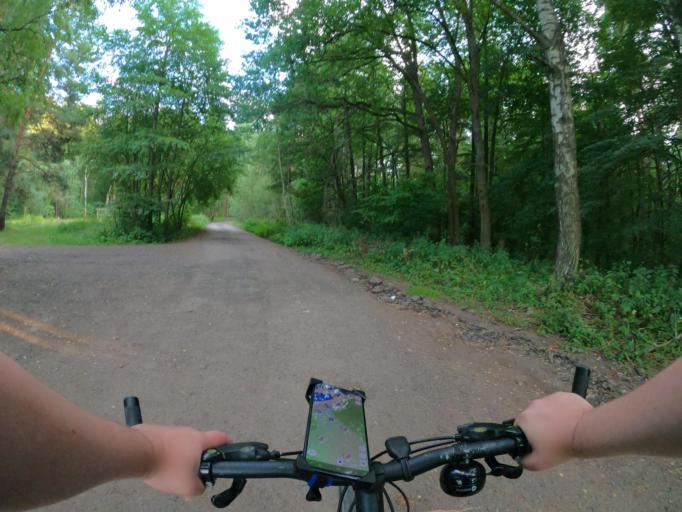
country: RU
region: Moskovskaya
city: Malyshevo
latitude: 55.5481
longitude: 38.3252
